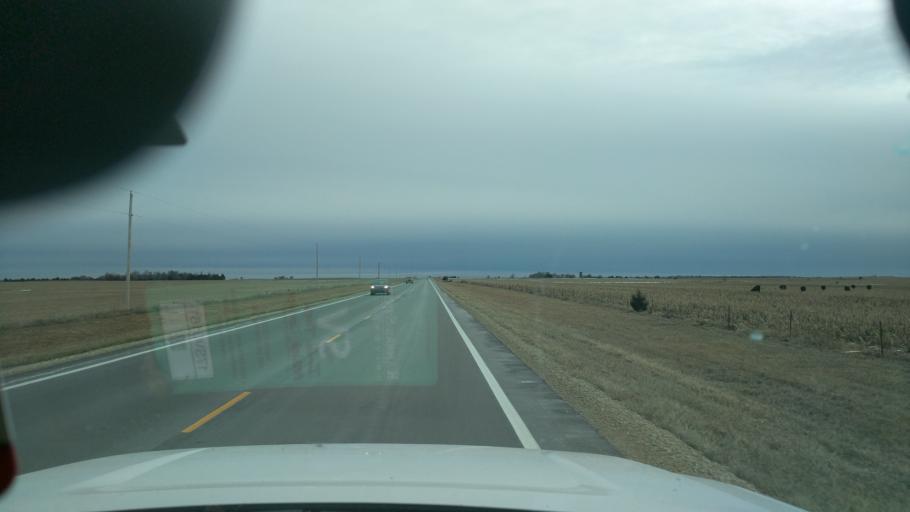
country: US
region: Kansas
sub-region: Geary County
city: Junction City
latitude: 38.8520
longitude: -96.8530
